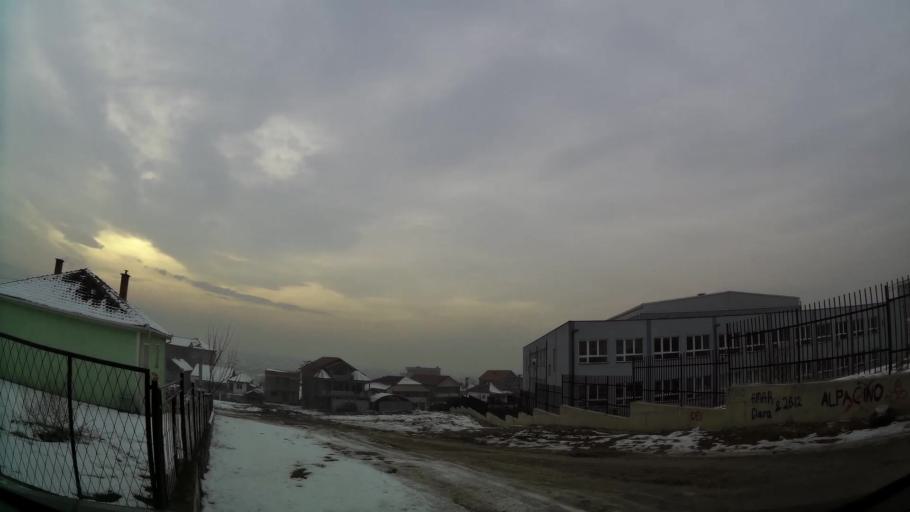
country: MK
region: Suto Orizari
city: Suto Orizare
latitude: 42.0389
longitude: 21.4279
